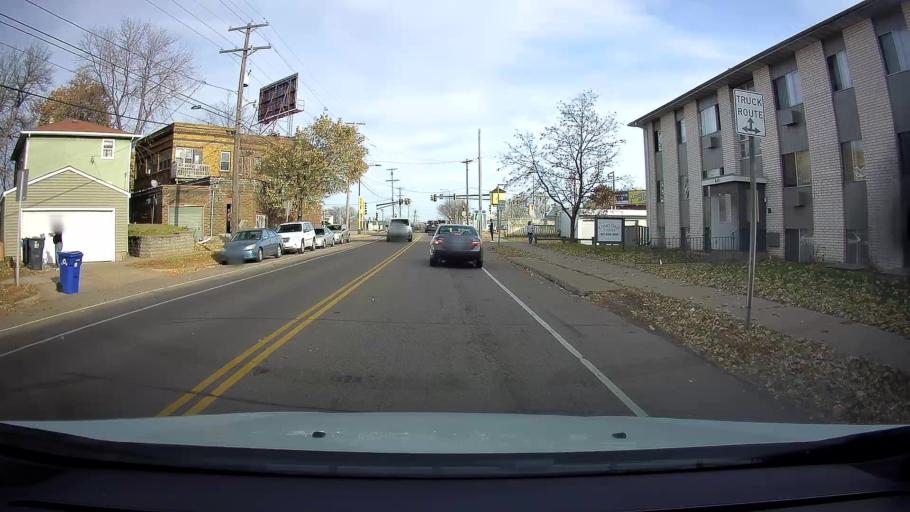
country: US
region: Minnesota
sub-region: Ramsey County
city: Saint Paul
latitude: 44.9701
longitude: -93.1276
